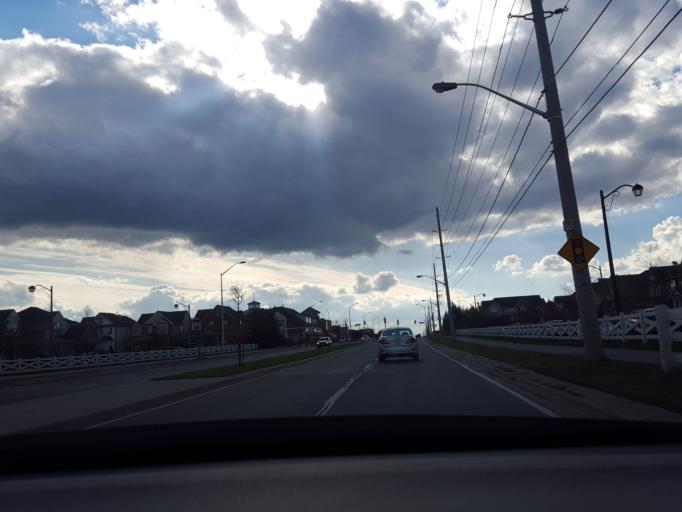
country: CA
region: Ontario
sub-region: Halton
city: Milton
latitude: 43.5300
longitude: -79.8361
